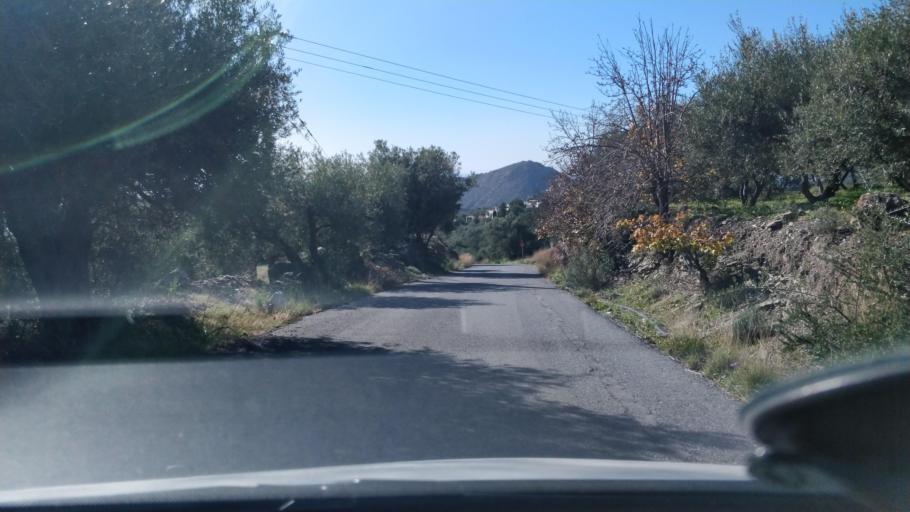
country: GR
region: Crete
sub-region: Nomos Lasithiou
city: Gra Liyia
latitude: 35.0216
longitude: 25.5574
